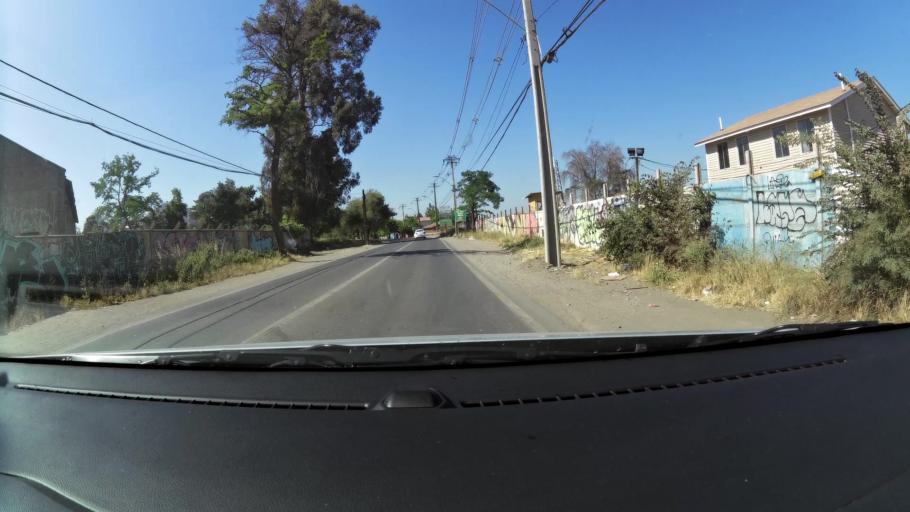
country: CL
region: Santiago Metropolitan
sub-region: Provincia de Maipo
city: San Bernardo
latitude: -33.6093
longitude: -70.6836
